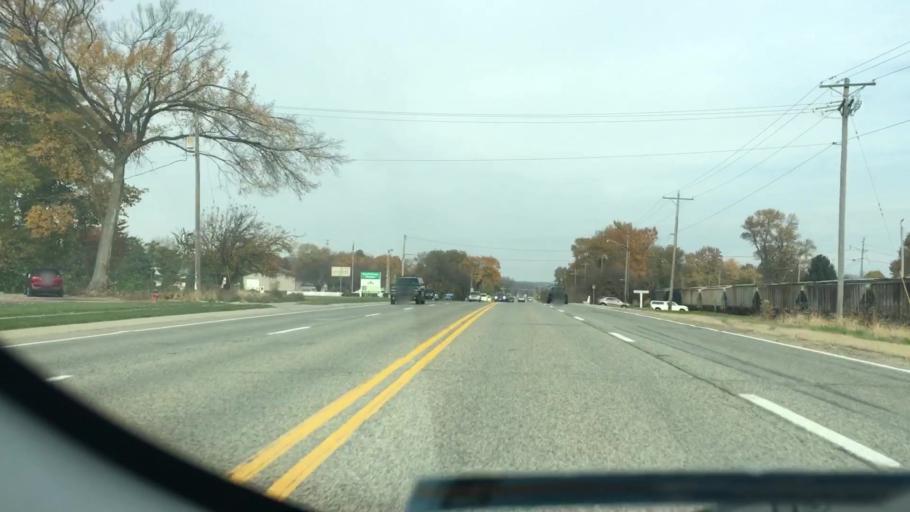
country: US
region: Illinois
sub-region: Peoria County
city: Peoria Heights
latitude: 40.7529
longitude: -89.5614
